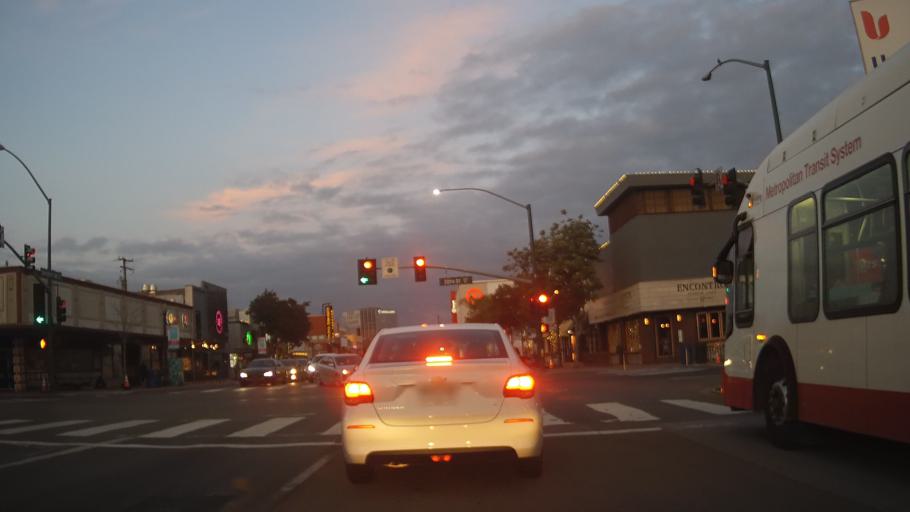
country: US
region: California
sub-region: San Diego County
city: San Diego
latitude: 32.7483
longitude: -117.1305
